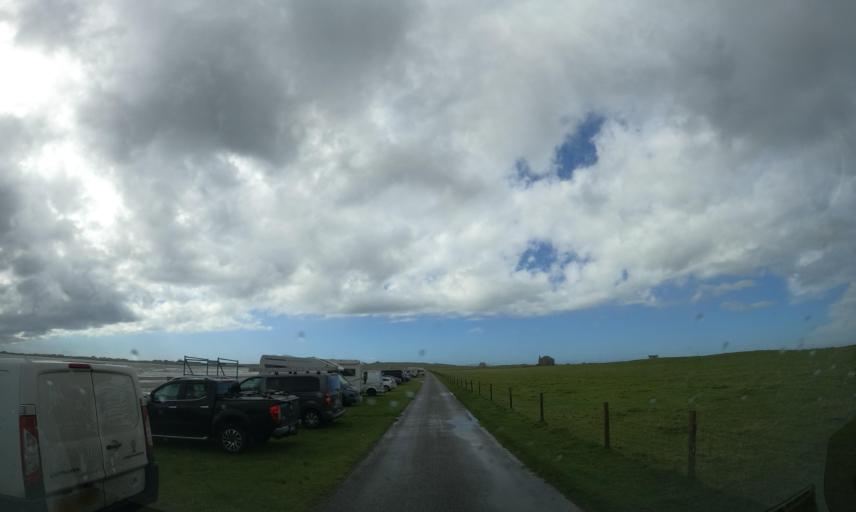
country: GB
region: Scotland
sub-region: Eilean Siar
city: Barra
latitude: 56.5219
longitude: -6.8081
